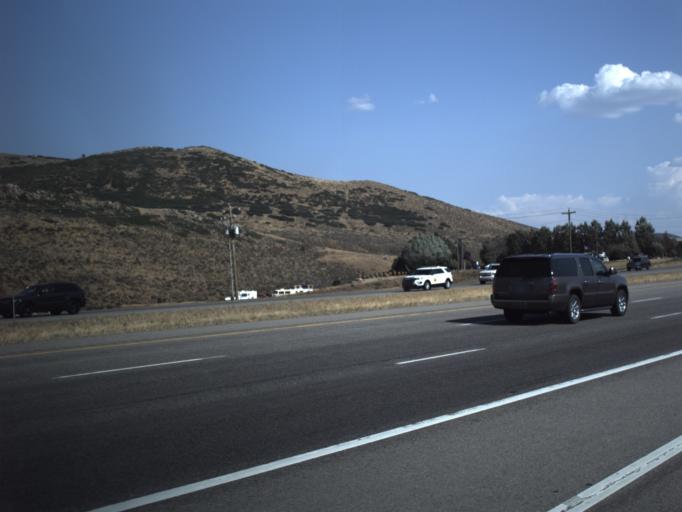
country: US
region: Utah
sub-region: Summit County
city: Snyderville
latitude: 40.7384
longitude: -111.5573
